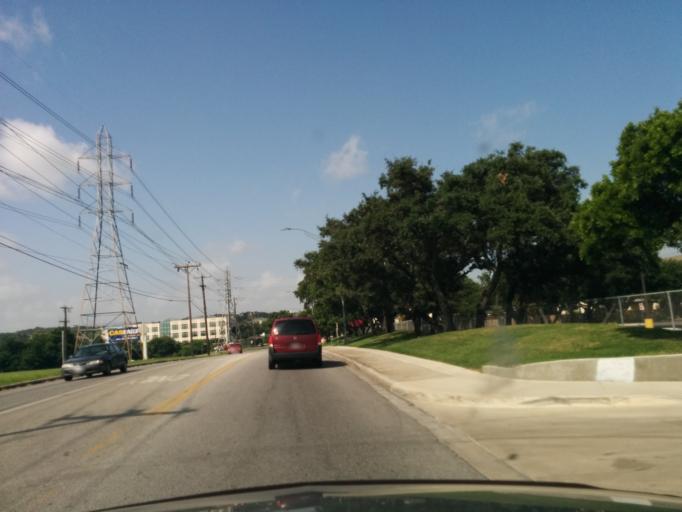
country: US
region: Texas
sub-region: Bexar County
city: Balcones Heights
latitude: 29.5218
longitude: -98.5572
